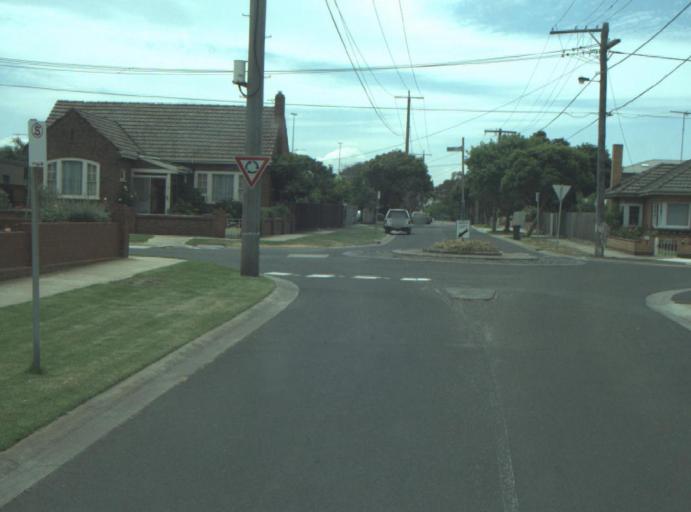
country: AU
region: Victoria
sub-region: Greater Geelong
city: Geelong West
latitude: -38.1220
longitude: 144.3568
